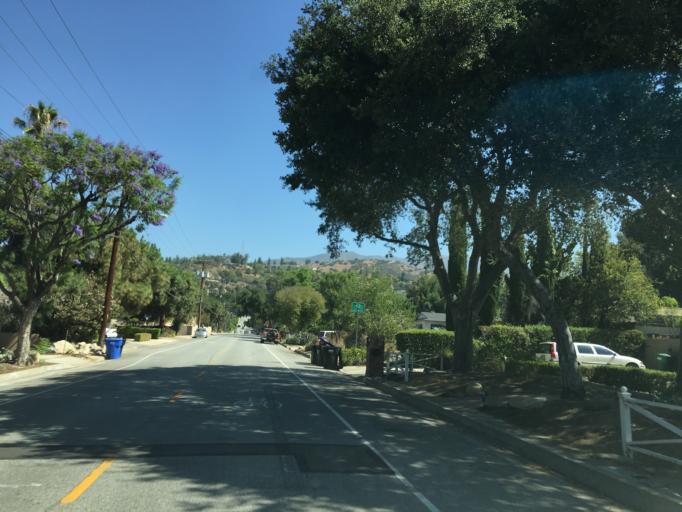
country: US
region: California
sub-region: Los Angeles County
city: Claremont
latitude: 34.1238
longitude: -117.7290
